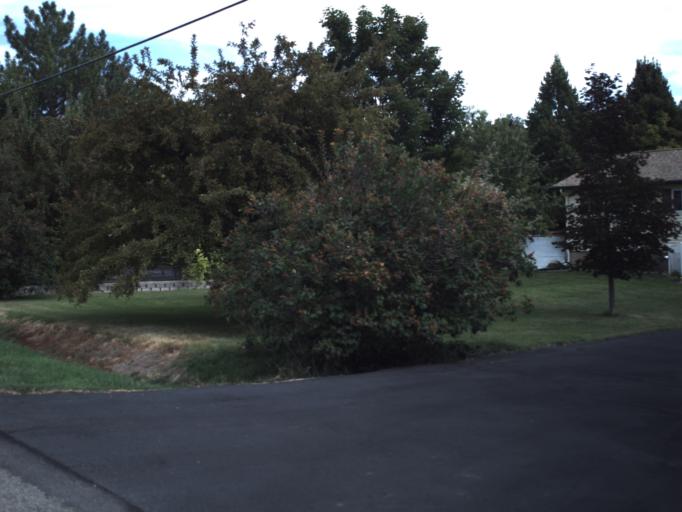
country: US
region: Utah
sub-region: Cache County
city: Mendon
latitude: 41.7181
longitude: -111.9790
